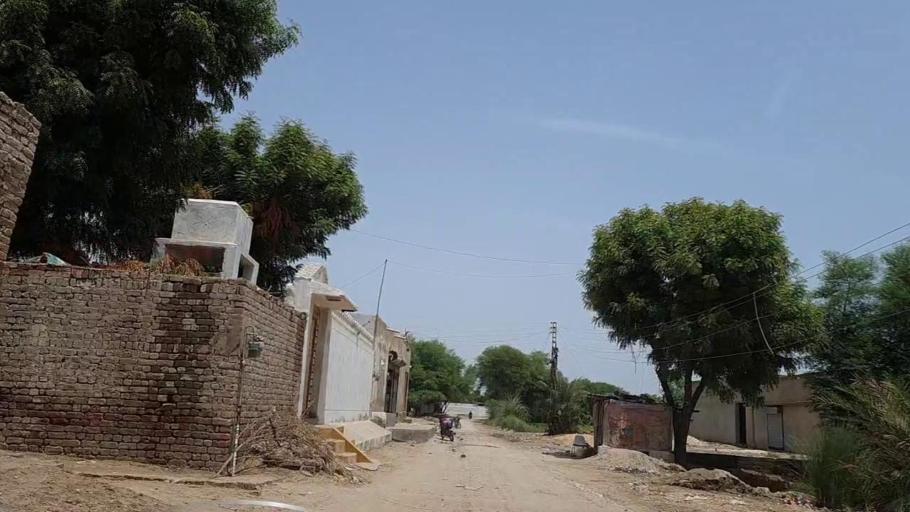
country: PK
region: Sindh
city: Tharu Shah
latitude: 26.9520
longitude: 68.0259
